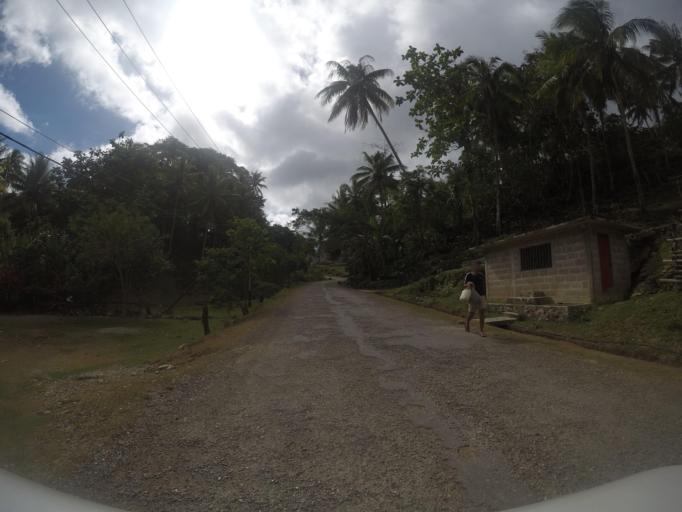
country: TL
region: Lautem
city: Lospalos
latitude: -8.5413
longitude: 126.9419
